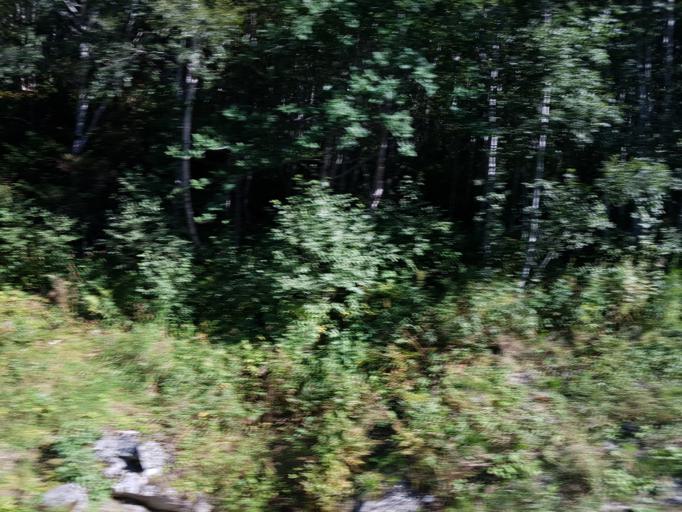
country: NO
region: Sor-Trondelag
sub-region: Afjord
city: A i Afjord
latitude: 63.7502
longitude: 10.2369
